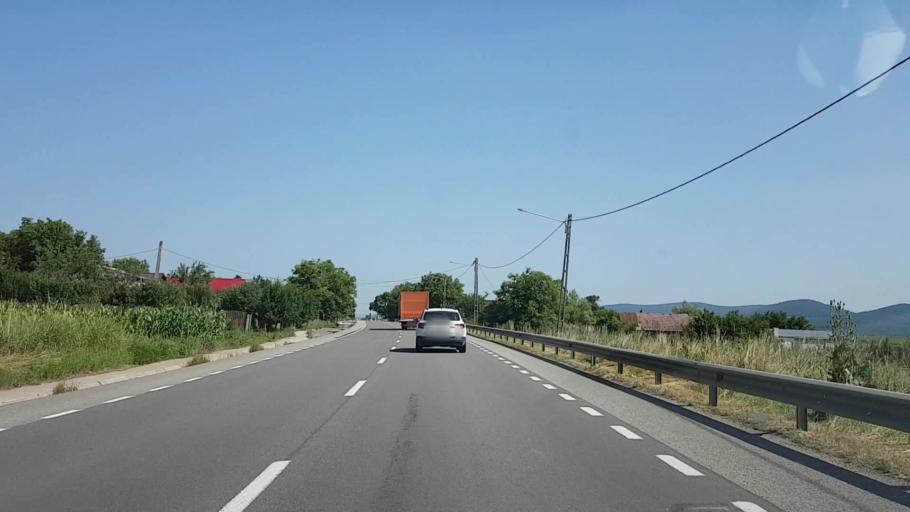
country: RO
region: Bistrita-Nasaud
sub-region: Comuna Sieu-Odorhei
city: Sieu-Odorhei
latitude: 47.1299
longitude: 24.3132
